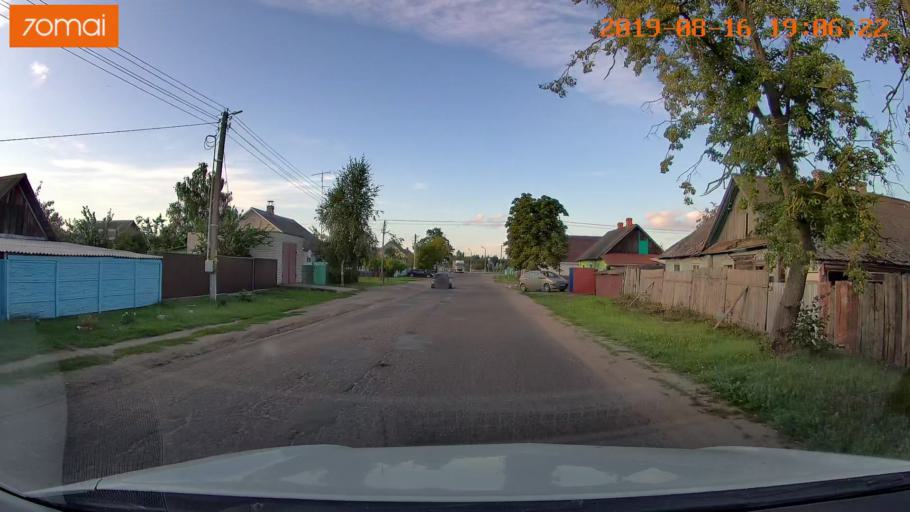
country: BY
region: Mogilev
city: Asipovichy
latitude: 53.2996
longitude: 28.6218
